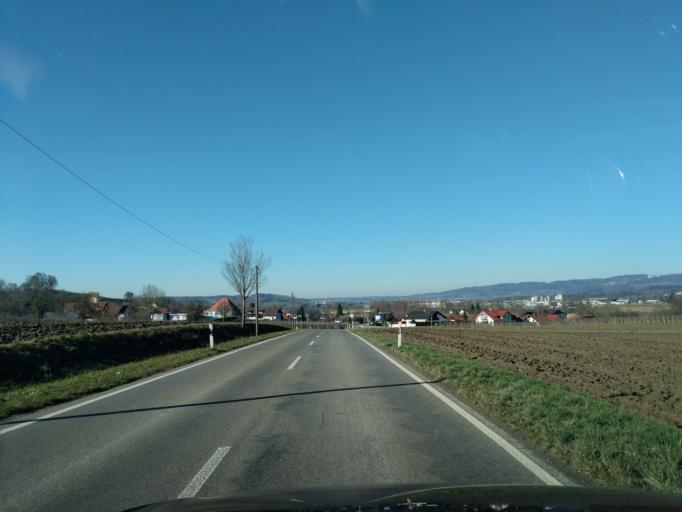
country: DE
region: Baden-Wuerttemberg
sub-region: Tuebingen Region
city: Salem
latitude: 47.7415
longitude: 9.3065
